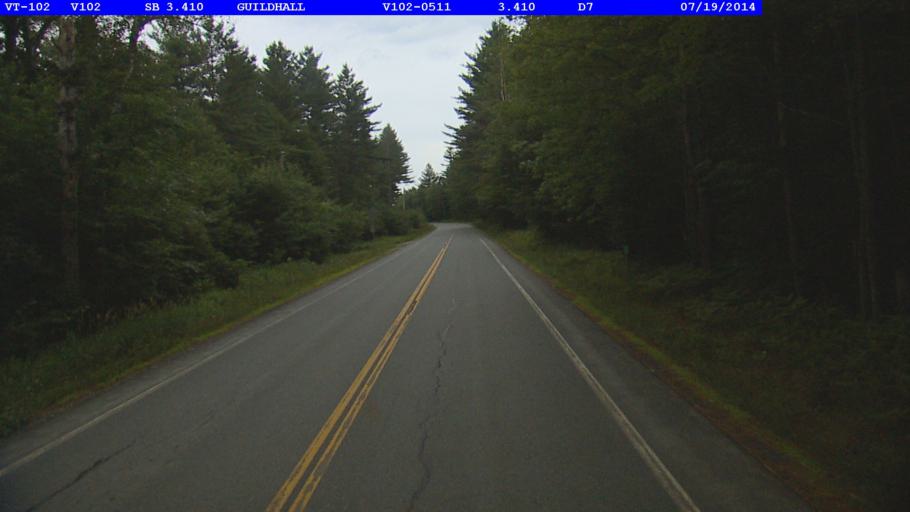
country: US
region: New Hampshire
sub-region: Coos County
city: Northumberland
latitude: 44.5422
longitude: -71.5834
